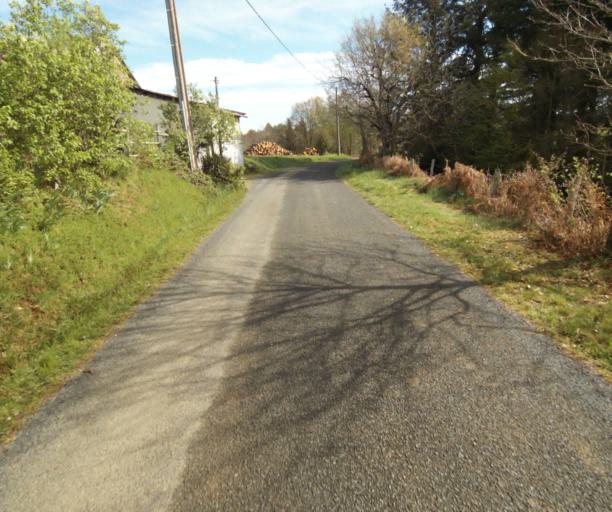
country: FR
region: Limousin
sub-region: Departement de la Correze
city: Laguenne
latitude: 45.2707
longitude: 1.8114
